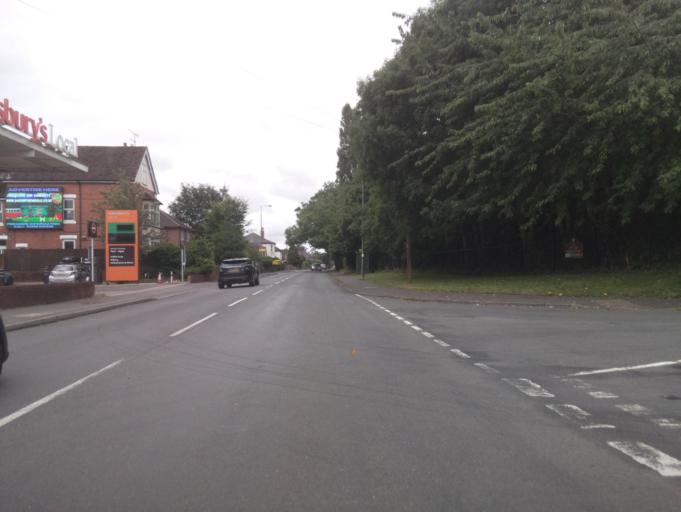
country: GB
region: England
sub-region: Worcestershire
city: Droitwich
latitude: 52.2604
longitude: -2.1535
